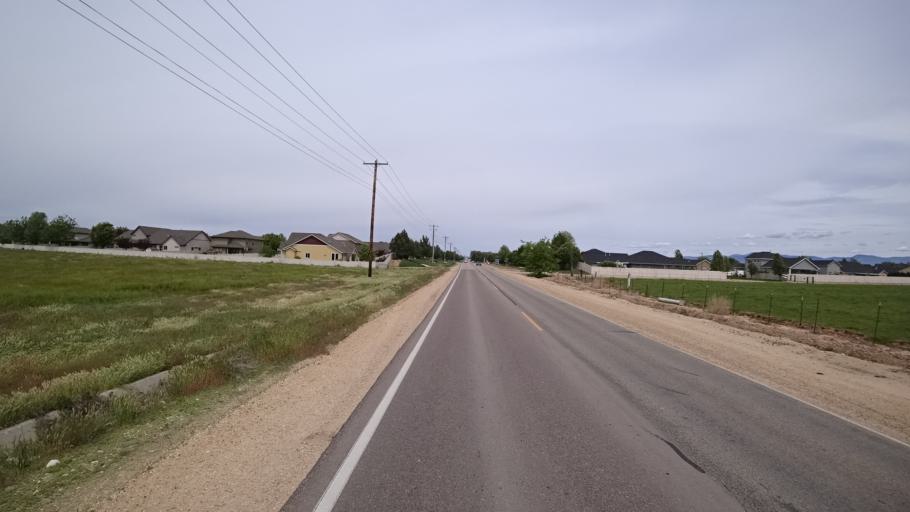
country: US
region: Idaho
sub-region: Ada County
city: Meridian
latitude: 43.5642
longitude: -116.3543
